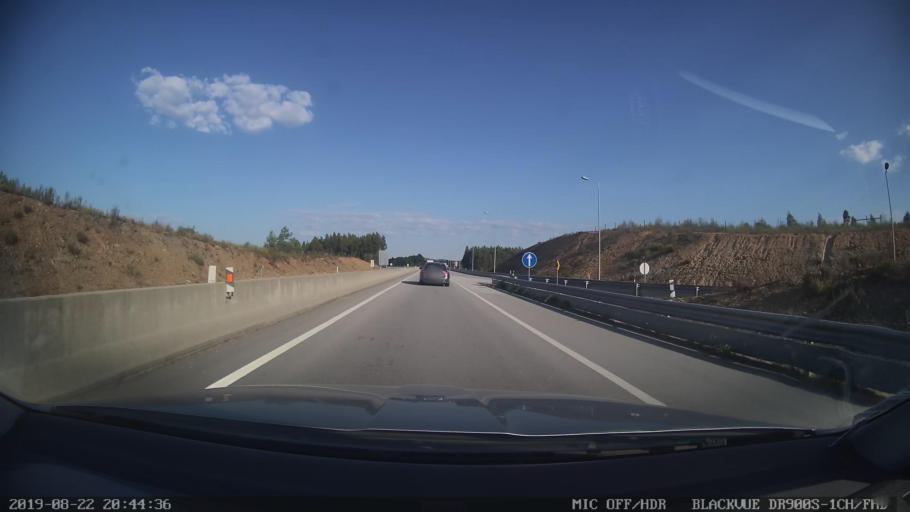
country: PT
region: Castelo Branco
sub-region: Proenca-A-Nova
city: Proenca-a-Nova
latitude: 39.7092
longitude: -7.8546
